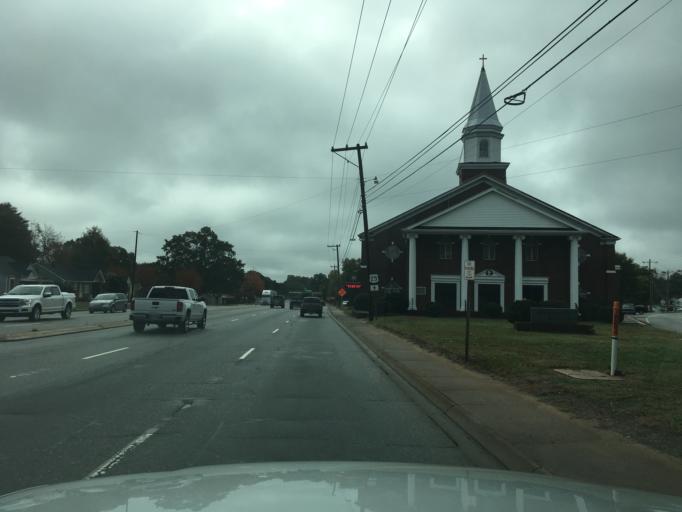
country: US
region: South Carolina
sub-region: Greenville County
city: Welcome
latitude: 34.8291
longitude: -82.4468
